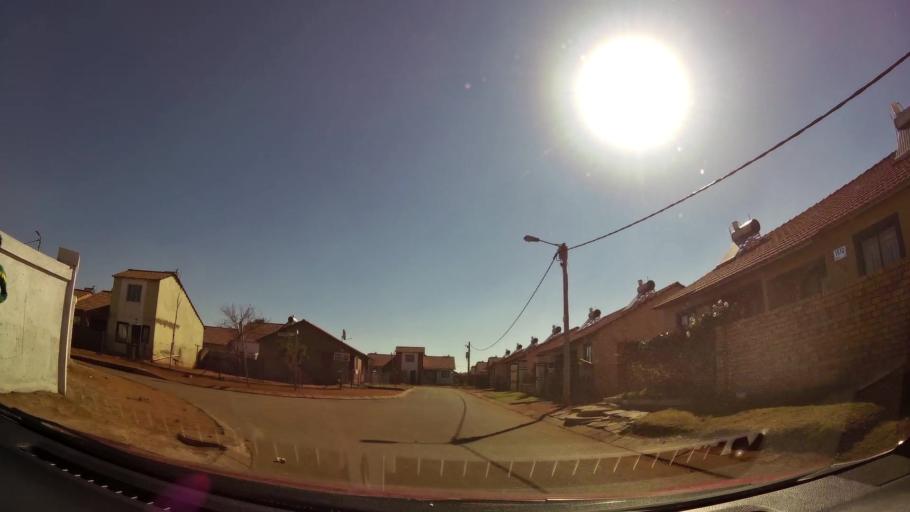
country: ZA
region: Gauteng
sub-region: City of Johannesburg Metropolitan Municipality
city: Soweto
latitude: -26.2362
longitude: 27.8021
